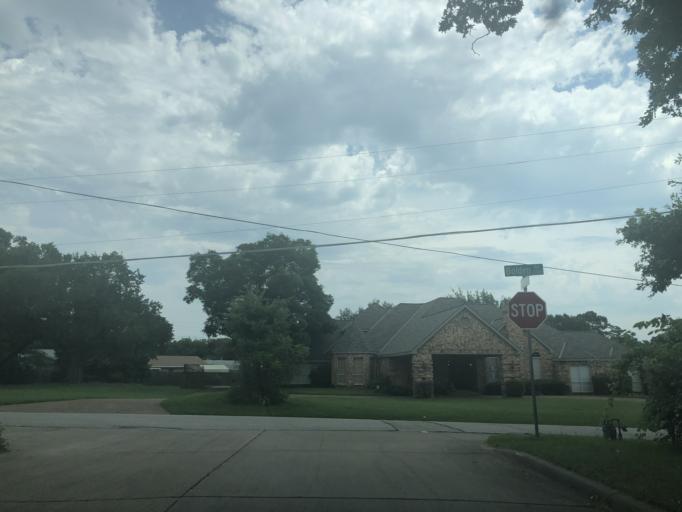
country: US
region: Texas
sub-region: Dallas County
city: Irving
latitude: 32.7903
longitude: -96.9410
